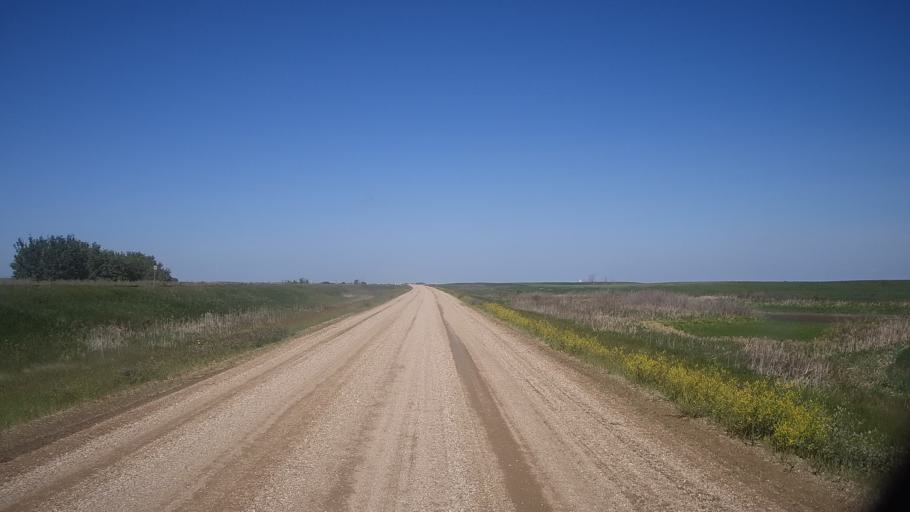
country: CA
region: Saskatchewan
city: Watrous
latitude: 51.8448
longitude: -105.9183
